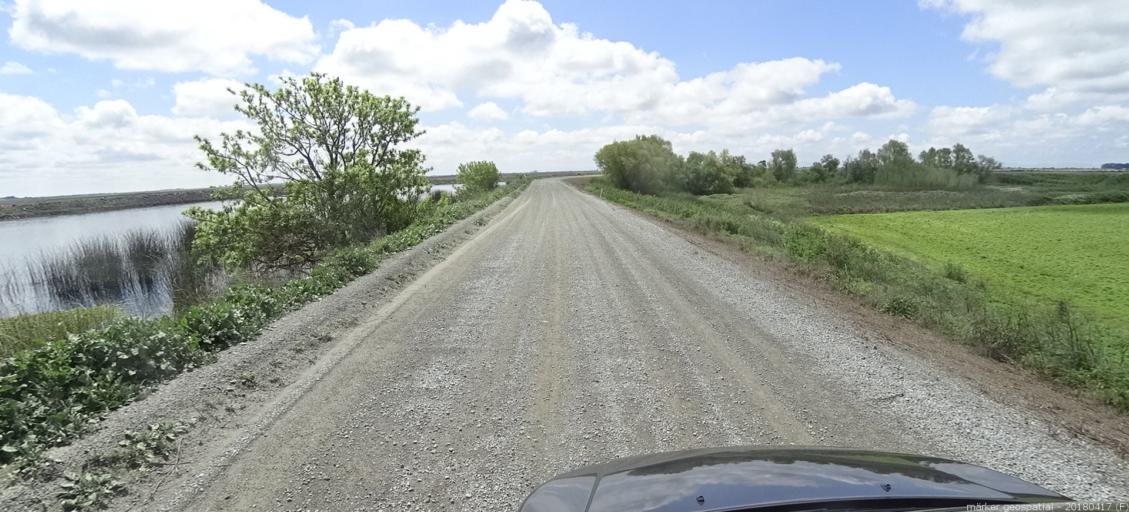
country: US
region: California
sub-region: Sacramento County
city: Walnut Grove
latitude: 38.1537
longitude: -121.5364
